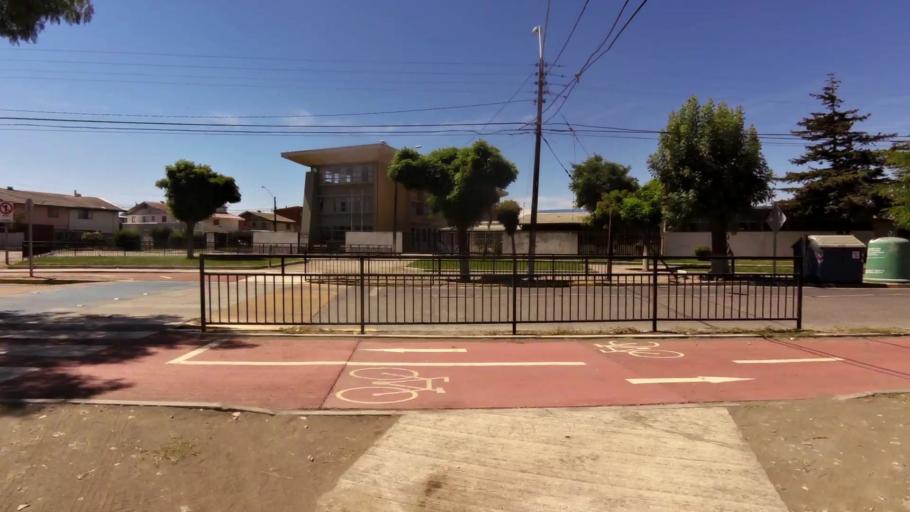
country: CL
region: Biobio
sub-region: Provincia de Concepcion
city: Talcahuano
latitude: -36.7604
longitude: -73.0943
